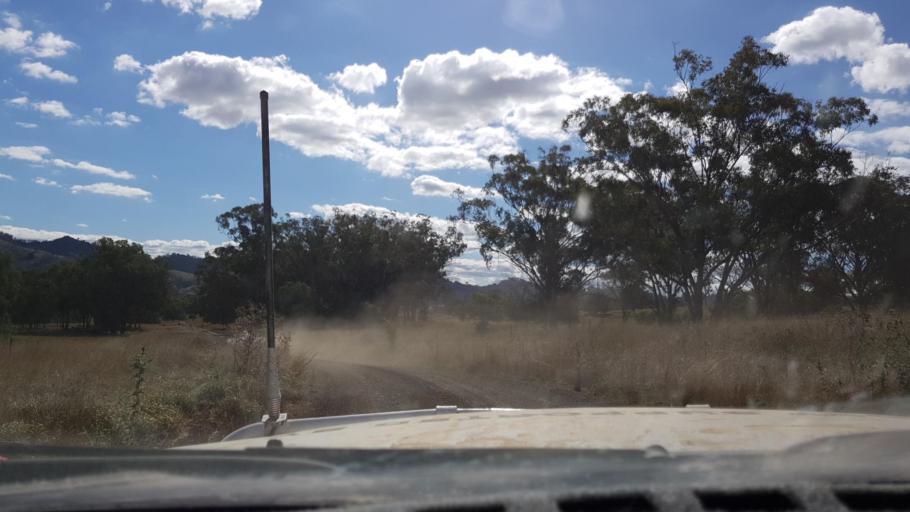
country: AU
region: New South Wales
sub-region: Tamworth Municipality
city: Manilla
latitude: -30.4616
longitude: 150.7804
